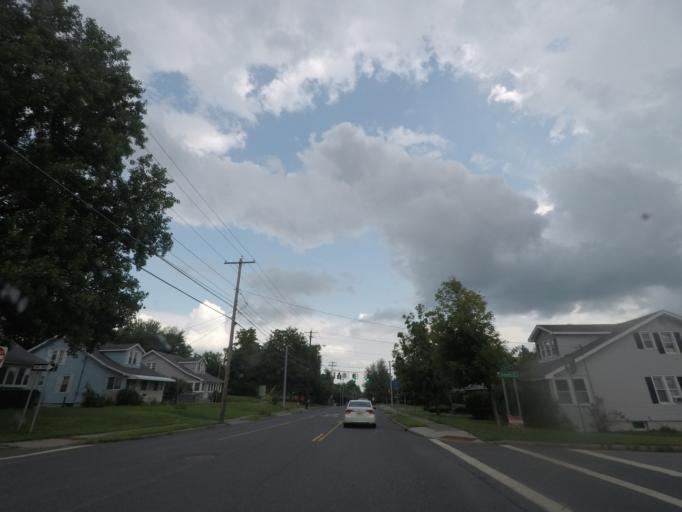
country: US
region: New York
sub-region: Albany County
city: Roessleville
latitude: 42.6972
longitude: -73.7914
